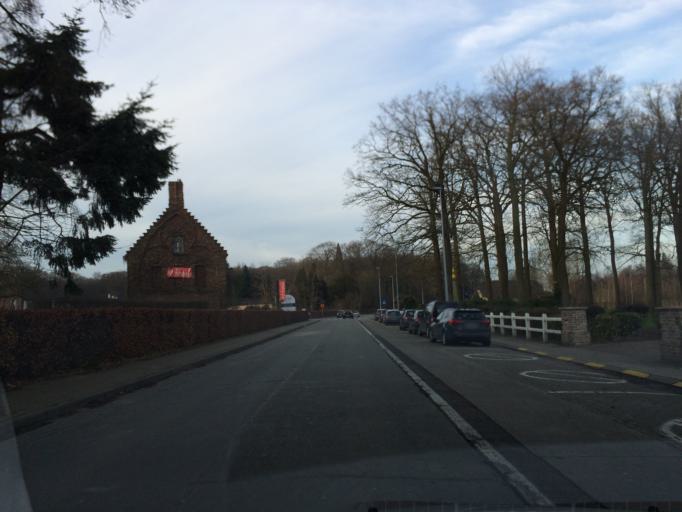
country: BE
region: Flanders
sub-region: Provincie West-Vlaanderen
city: Roeselare
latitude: 50.9255
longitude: 3.1392
